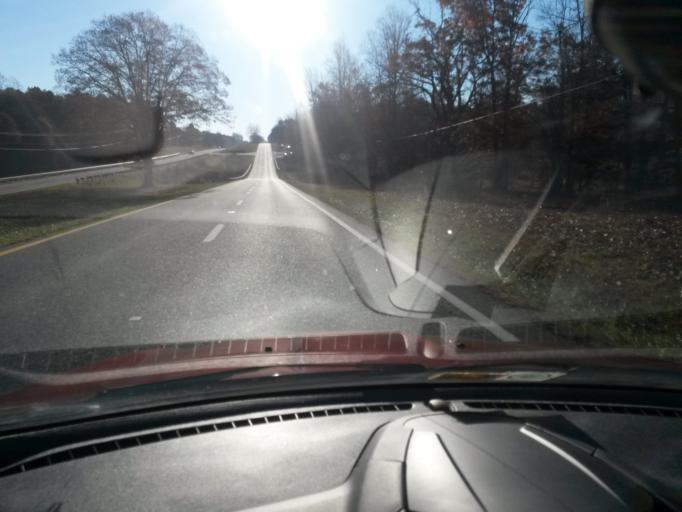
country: US
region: Virginia
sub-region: Appomattox County
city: Appomattox
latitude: 37.2997
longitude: -78.7431
